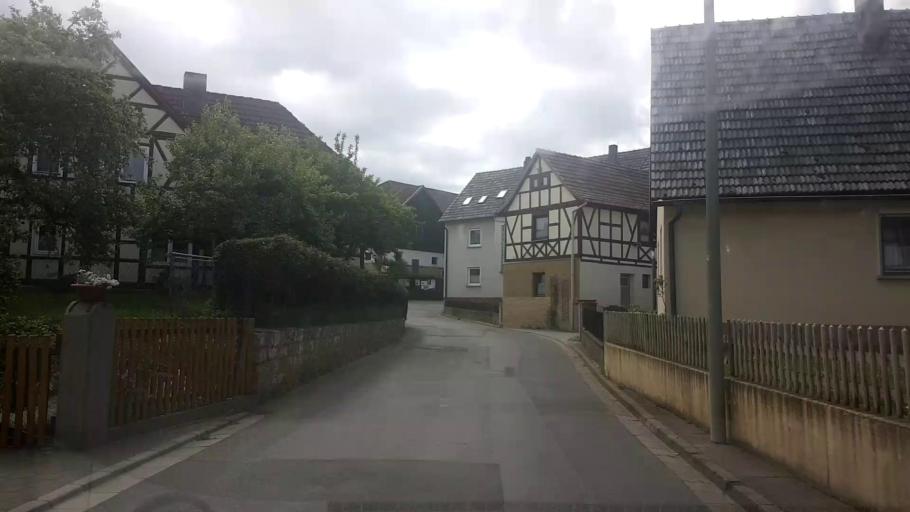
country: DE
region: Bavaria
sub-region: Upper Franconia
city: Bad Staffelstein
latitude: 50.1150
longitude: 11.0313
